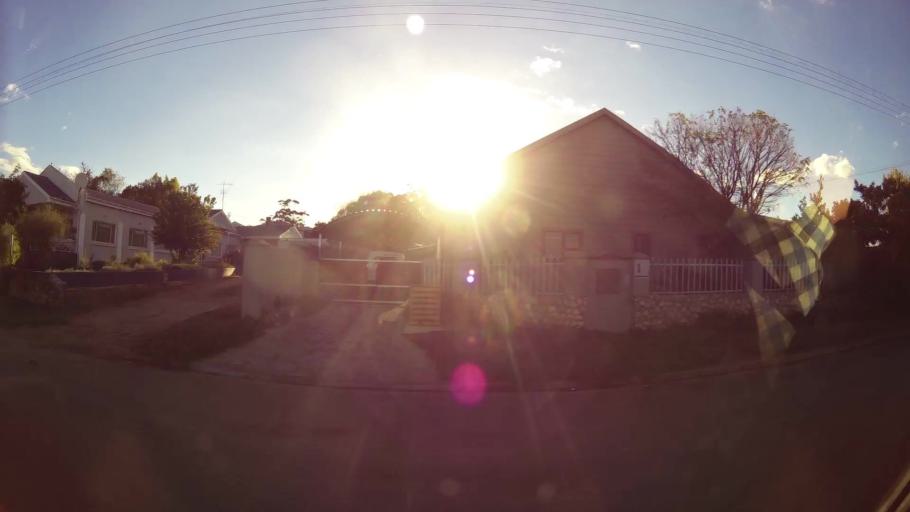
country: ZA
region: Western Cape
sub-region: Eden District Municipality
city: Riversdale
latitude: -34.0852
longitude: 20.9580
